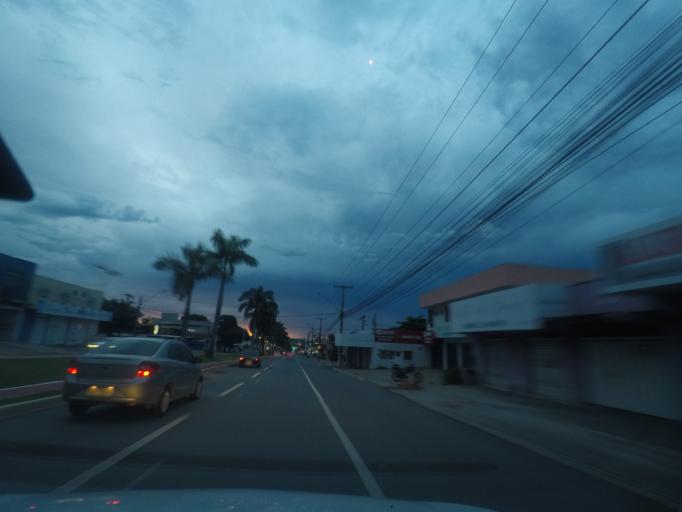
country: BR
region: Goias
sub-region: Goiania
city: Goiania
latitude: -16.7160
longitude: -49.2847
